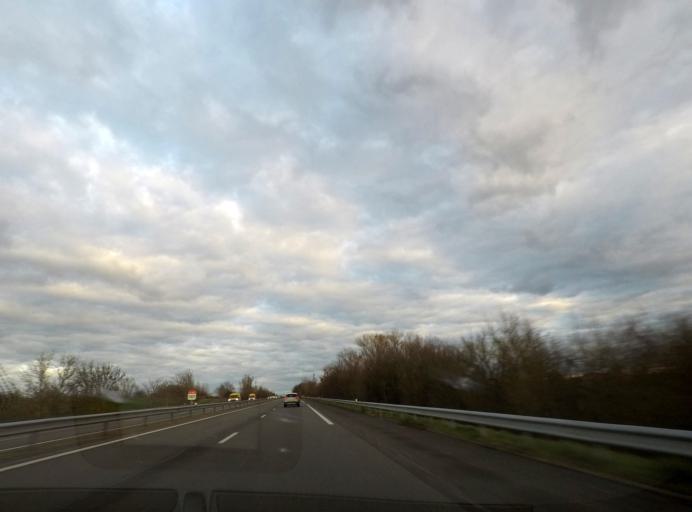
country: FR
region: Rhone-Alpes
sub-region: Departement de l'Ain
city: Mezeriat
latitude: 46.2701
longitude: 5.0361
